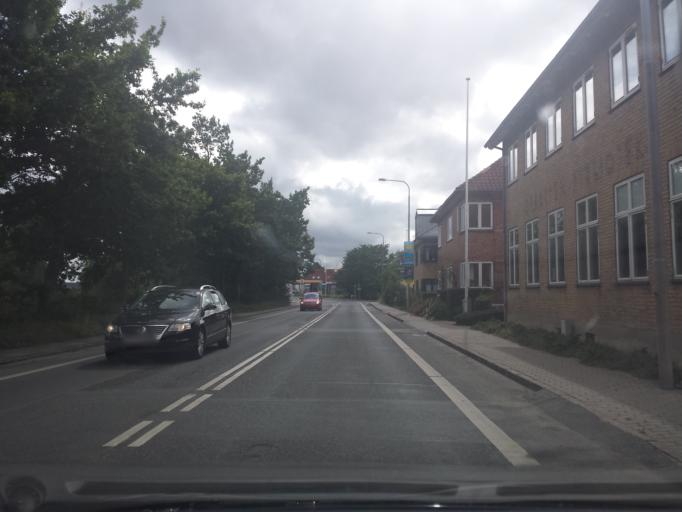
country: DK
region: South Denmark
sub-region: Sonderborg Kommune
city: Grasten
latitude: 54.9202
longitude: 9.5959
